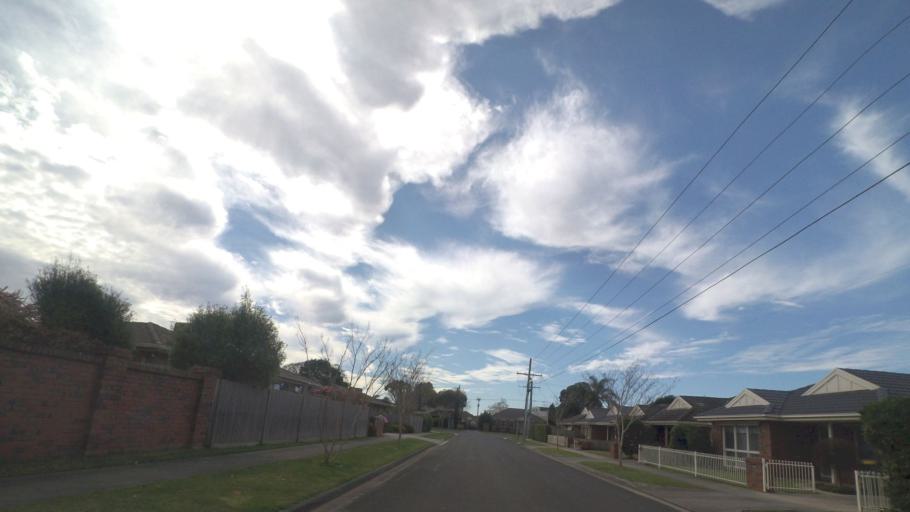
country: AU
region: Victoria
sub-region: Knox
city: Bayswater
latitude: -37.8445
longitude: 145.2634
